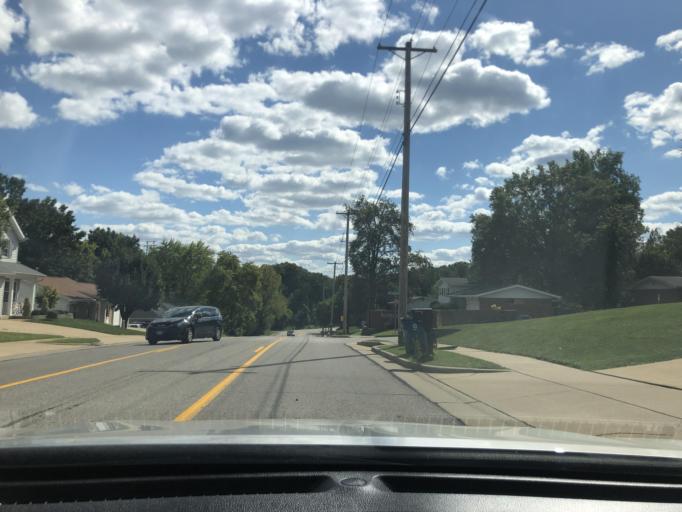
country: US
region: Missouri
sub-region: Saint Louis County
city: Green Park
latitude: 38.5088
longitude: -90.3430
